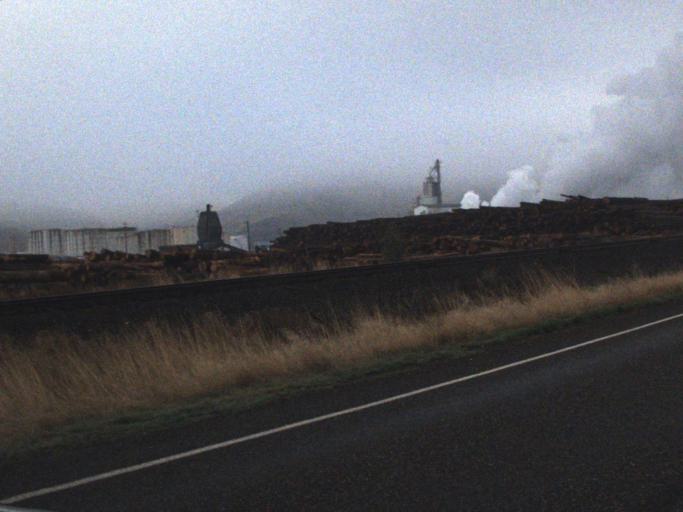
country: US
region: Washington
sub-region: Asotin County
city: Clarkston Heights-Vineland
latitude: 46.4257
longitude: -117.1064
